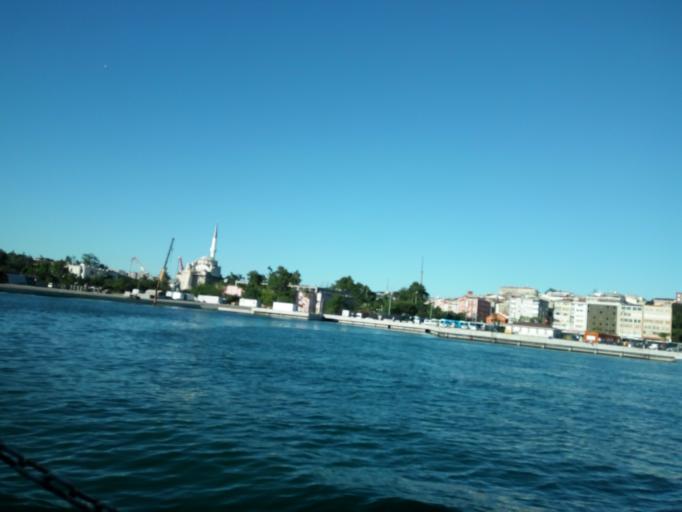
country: TR
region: Istanbul
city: UEskuedar
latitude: 40.9949
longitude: 29.0212
